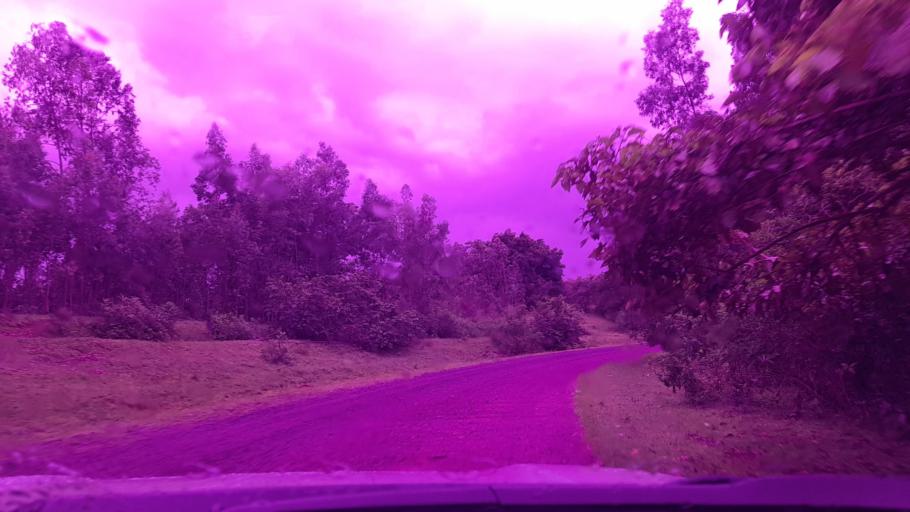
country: ET
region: Oromiya
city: Metu
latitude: 8.4327
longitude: 35.6138
